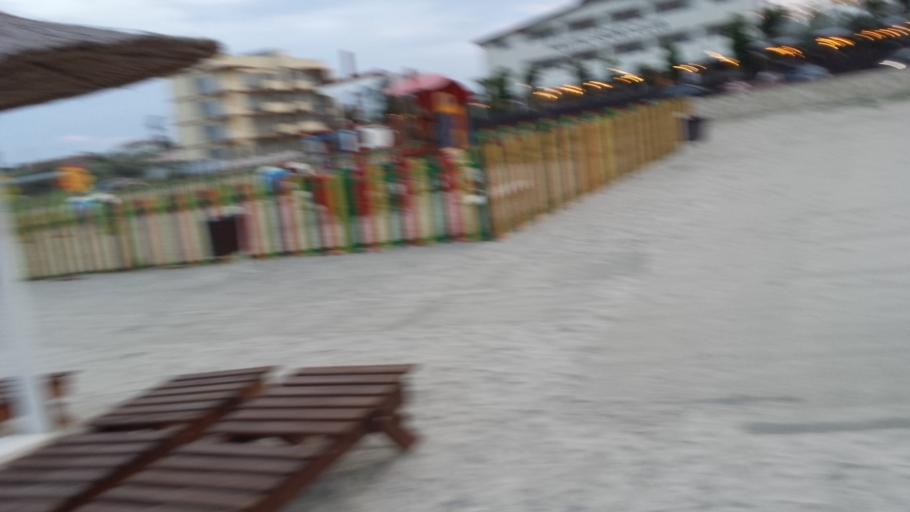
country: RO
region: Constanta
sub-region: Comuna Navodari
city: Navodari
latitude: 44.3205
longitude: 28.6362
